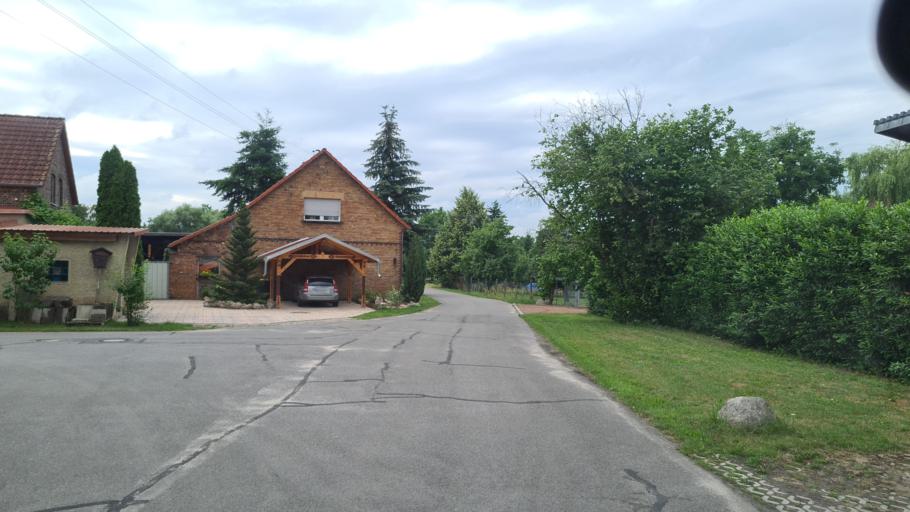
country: DE
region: Brandenburg
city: Bronkow
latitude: 51.7015
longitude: 13.8767
